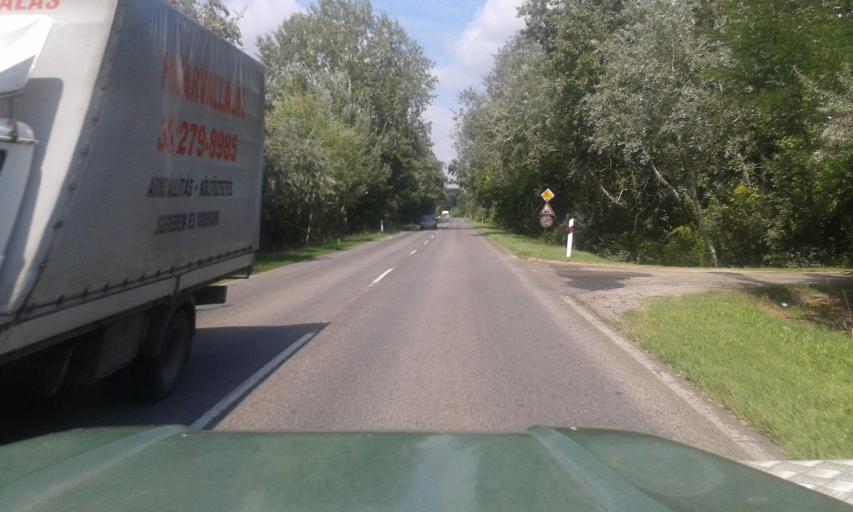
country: HU
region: Csongrad
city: Szatymaz
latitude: 46.3385
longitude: 20.0660
